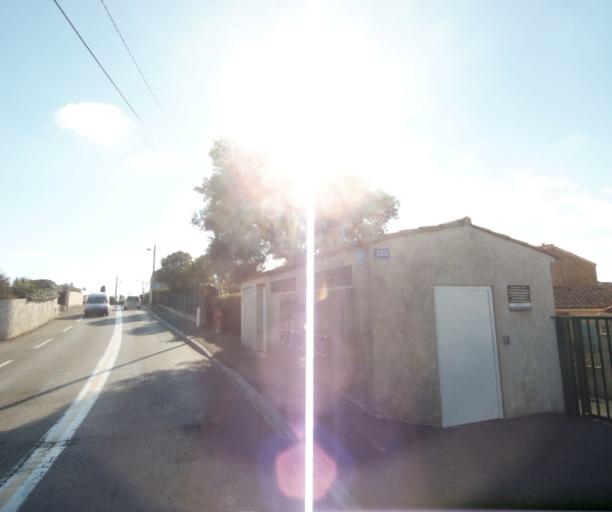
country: FR
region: Provence-Alpes-Cote d'Azur
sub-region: Departement des Alpes-Maritimes
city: Biot
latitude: 43.6016
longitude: 7.1064
